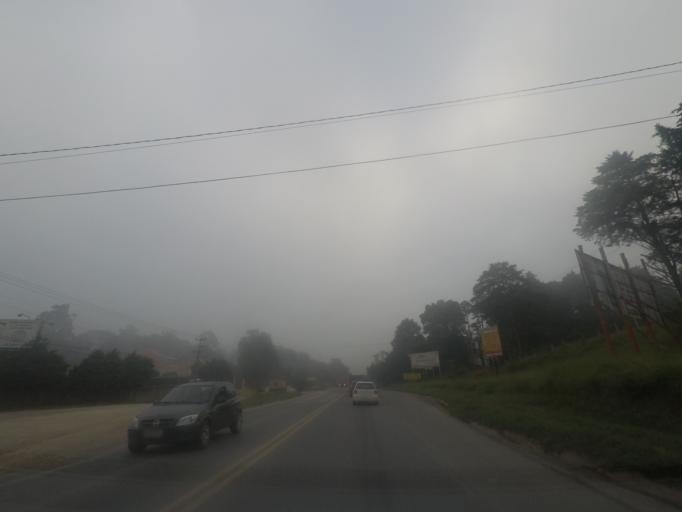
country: BR
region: Parana
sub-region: Almirante Tamandare
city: Almirante Tamandare
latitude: -25.3023
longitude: -49.3040
